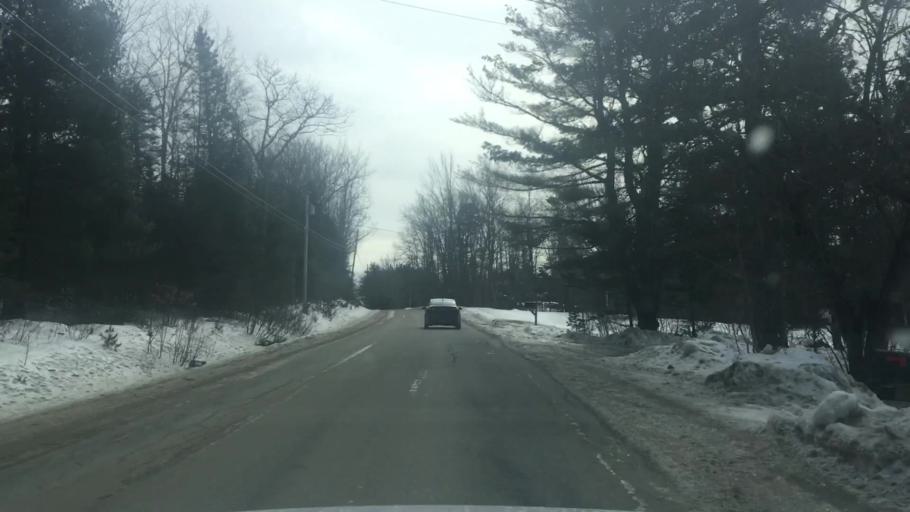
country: US
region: Maine
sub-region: Hancock County
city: Orland
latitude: 44.5859
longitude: -68.7259
